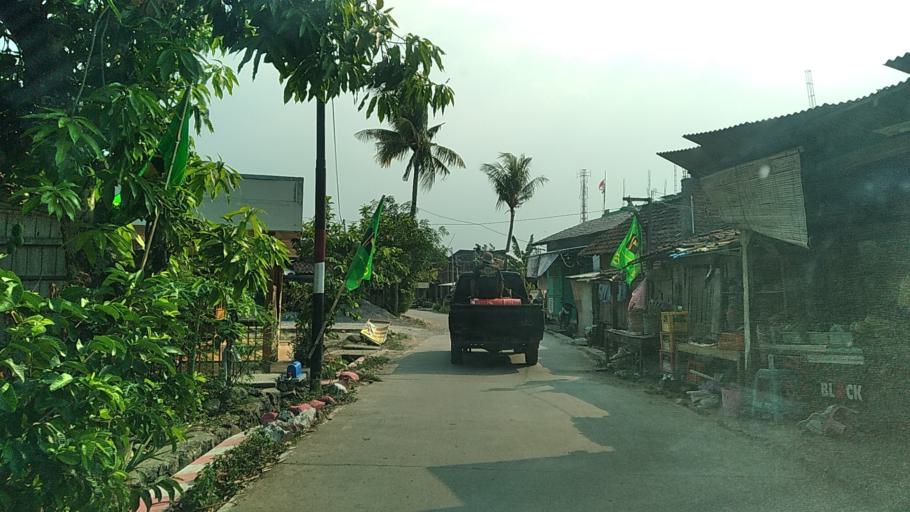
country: ID
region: Central Java
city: Mranggen
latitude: -7.0786
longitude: 110.4657
